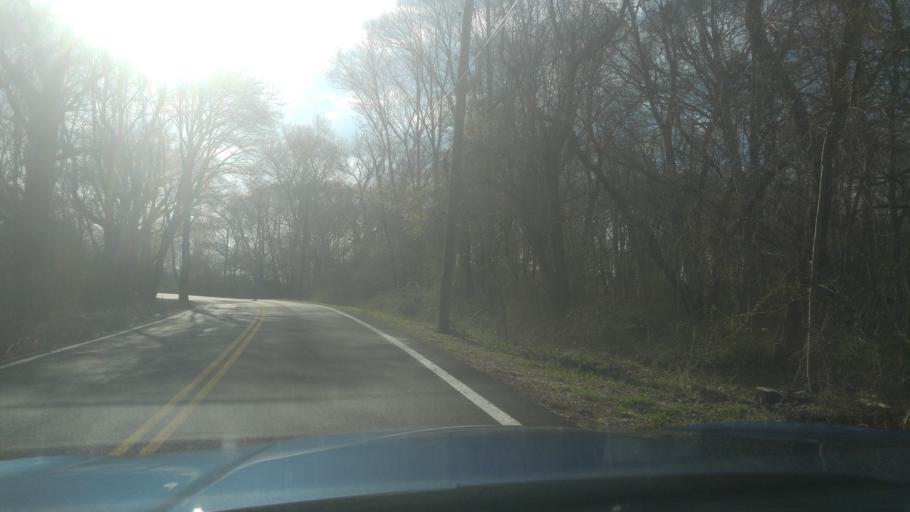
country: US
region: Rhode Island
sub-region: Newport County
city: Jamestown
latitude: 41.5715
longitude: -71.3703
